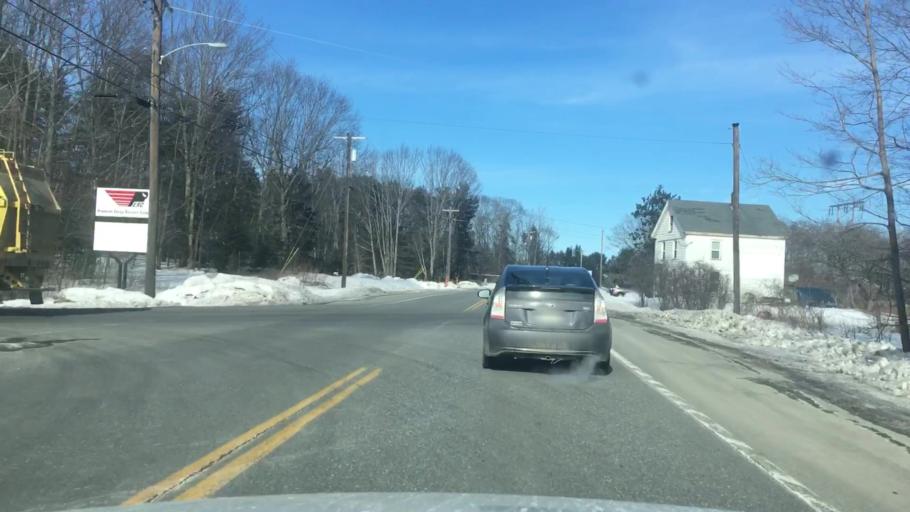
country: US
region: Maine
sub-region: Penobscot County
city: Orrington
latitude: 44.7370
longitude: -68.8207
